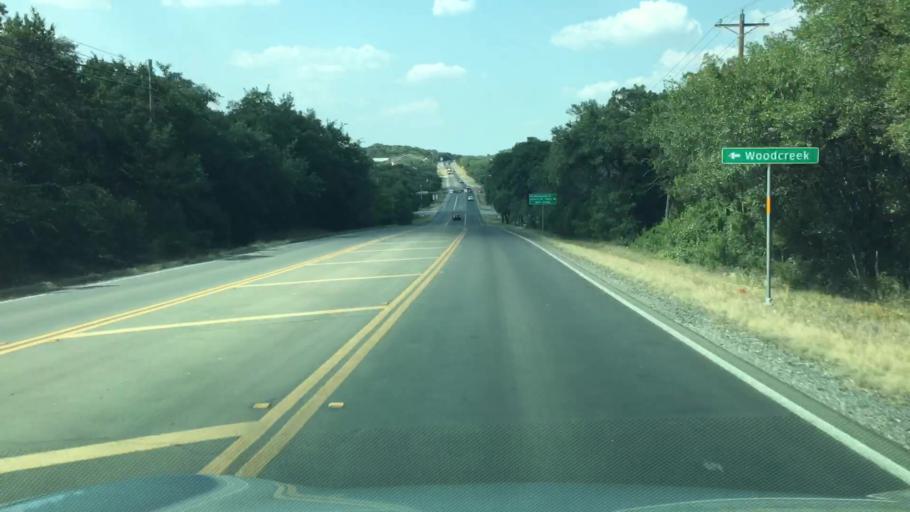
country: US
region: Texas
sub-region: Hays County
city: Woodcreek
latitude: 30.0250
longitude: -98.1015
